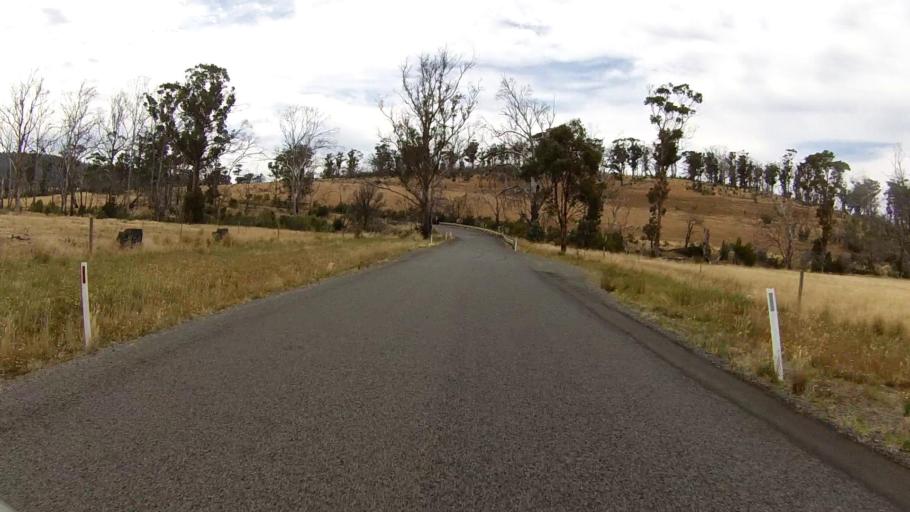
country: AU
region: Tasmania
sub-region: Sorell
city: Sorell
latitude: -42.8952
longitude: 147.7776
